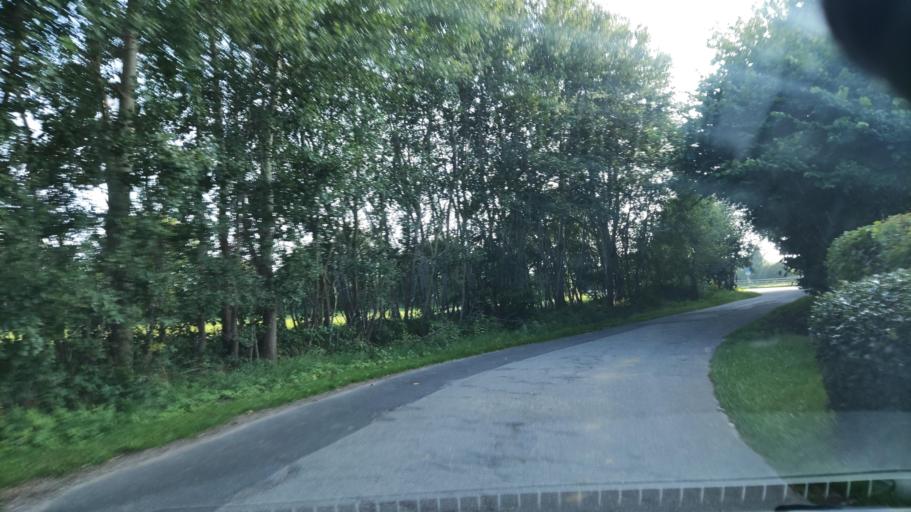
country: DE
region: Schleswig-Holstein
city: Struvenhutten
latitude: 53.8590
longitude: 10.0699
